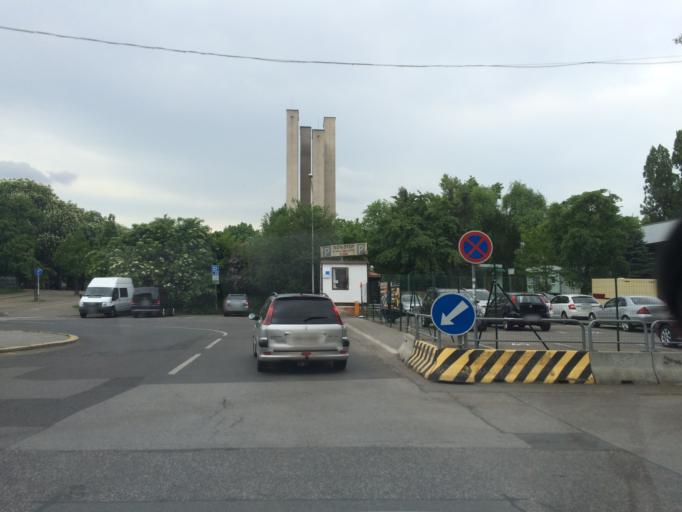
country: CZ
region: Praha
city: Prague
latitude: 50.0972
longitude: 14.4241
